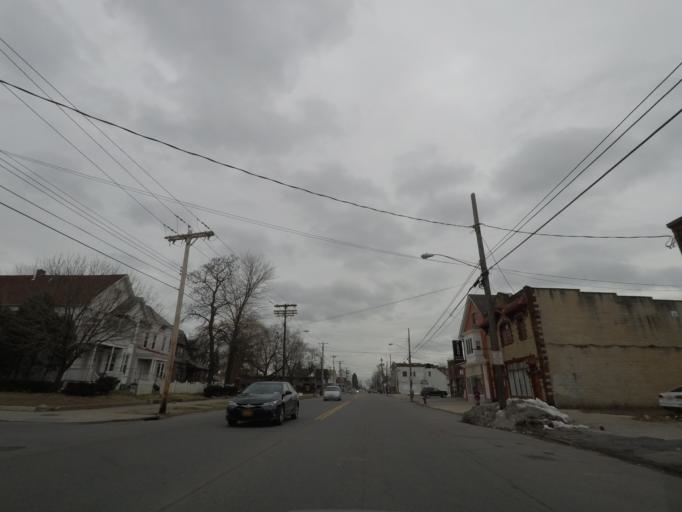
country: US
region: New York
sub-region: Schenectady County
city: Schenectady
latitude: 42.8062
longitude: -73.9332
